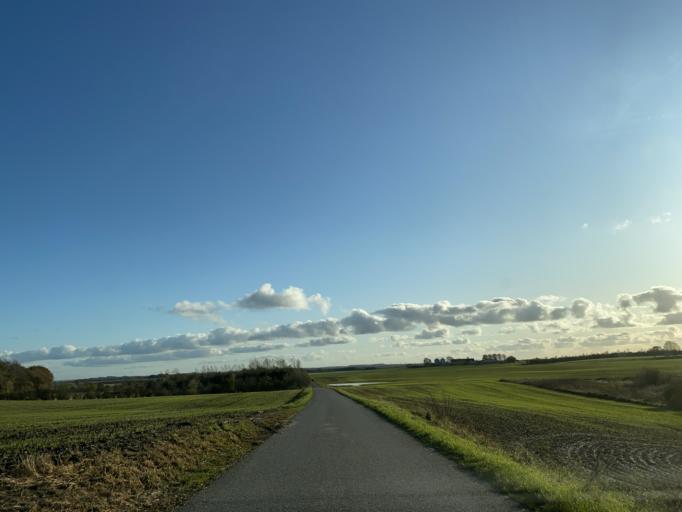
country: DK
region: Central Jutland
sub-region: Viborg Kommune
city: Bjerringbro
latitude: 56.3419
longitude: 9.7145
